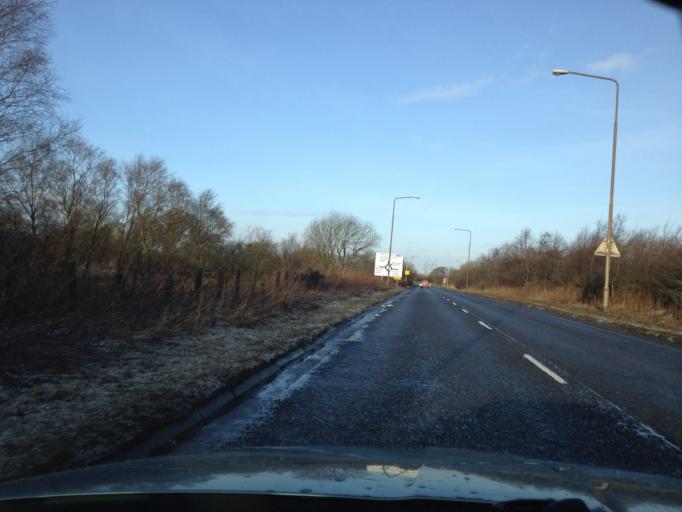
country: GB
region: Scotland
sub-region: West Lothian
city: Blackburn
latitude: 55.8782
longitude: -3.6576
